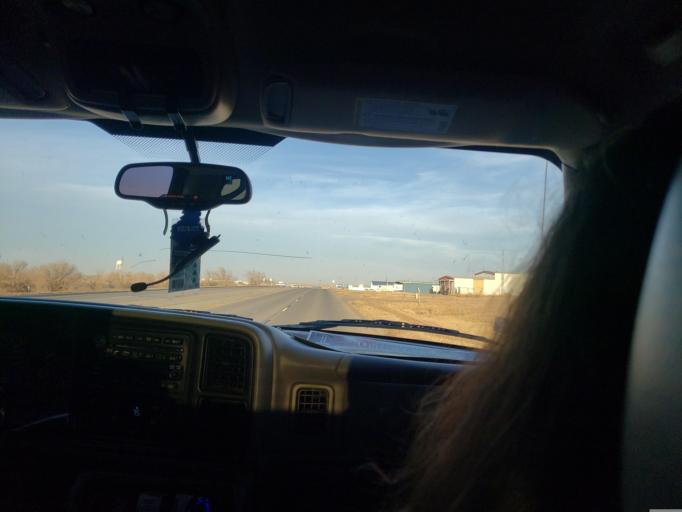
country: US
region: Oklahoma
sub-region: Texas County
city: Guymon
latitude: 36.6990
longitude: -101.4547
